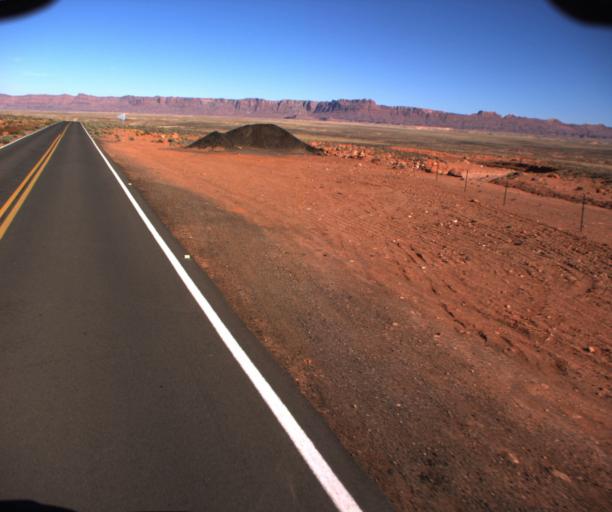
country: US
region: Arizona
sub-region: Coconino County
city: LeChee
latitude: 36.6994
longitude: -111.8008
